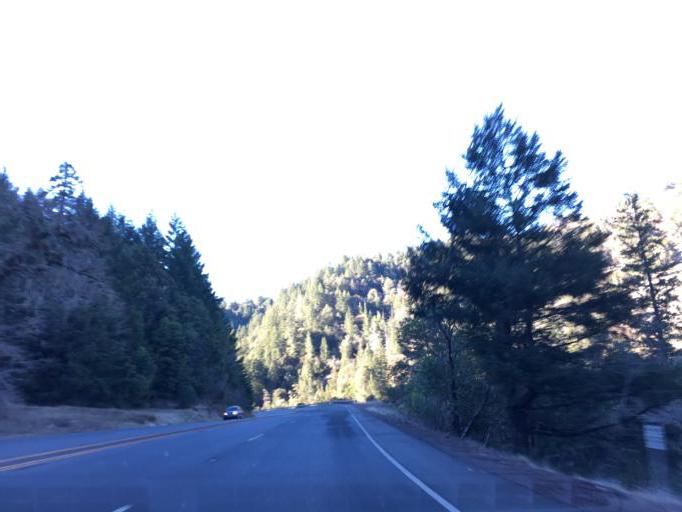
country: US
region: California
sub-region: Mendocino County
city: Laytonville
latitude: 39.8270
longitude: -123.5843
